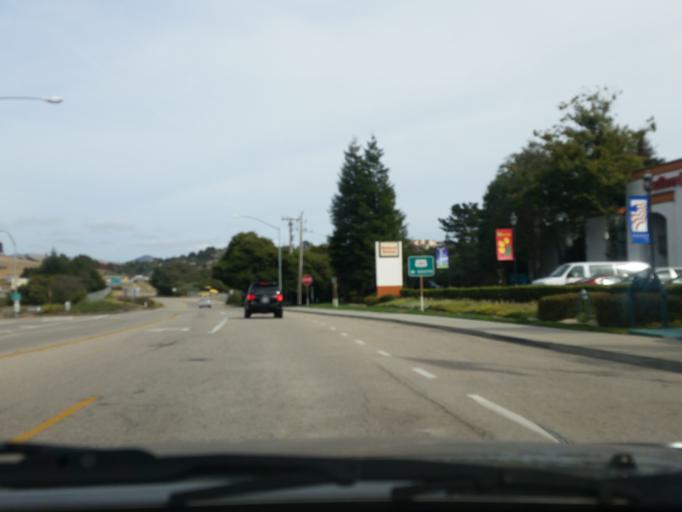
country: US
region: California
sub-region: San Luis Obispo County
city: Grover Beach
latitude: 35.1348
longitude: -120.6203
